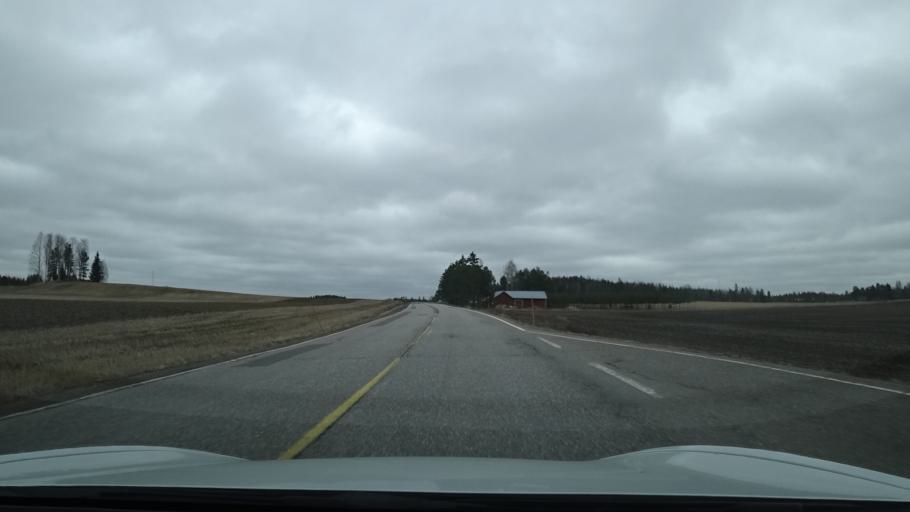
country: FI
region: Uusimaa
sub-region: Porvoo
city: Myrskylae
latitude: 60.6591
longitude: 25.8126
